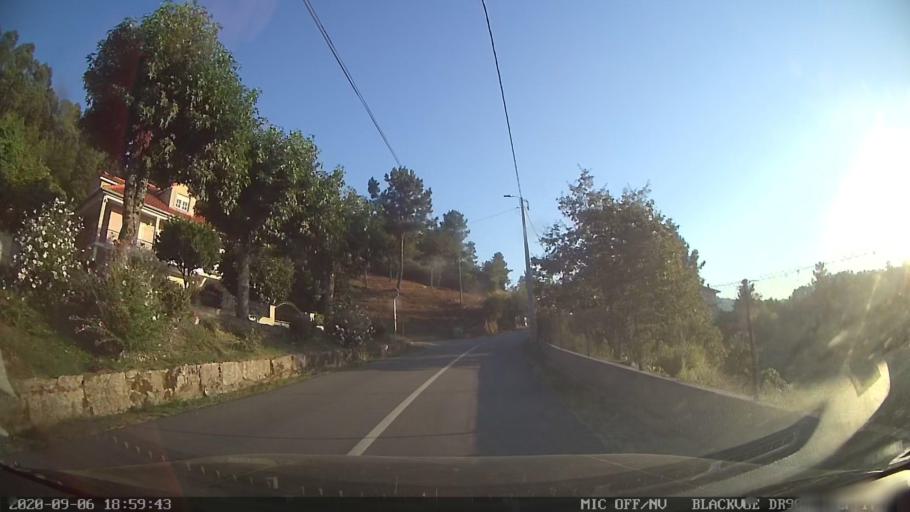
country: PT
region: Porto
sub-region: Baiao
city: Baiao
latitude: 41.2414
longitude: -7.9962
